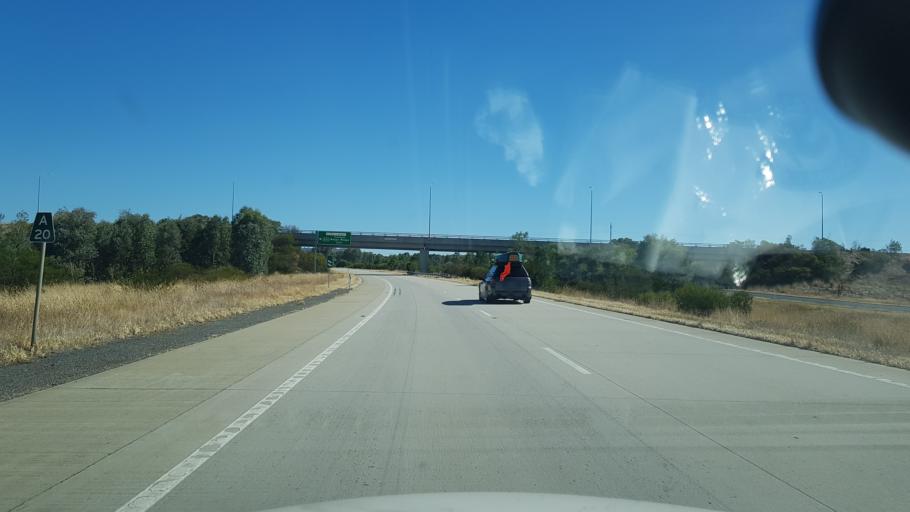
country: AU
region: New South Wales
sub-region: Greater Hume Shire
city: Jindera
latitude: -35.9259
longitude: 147.0086
